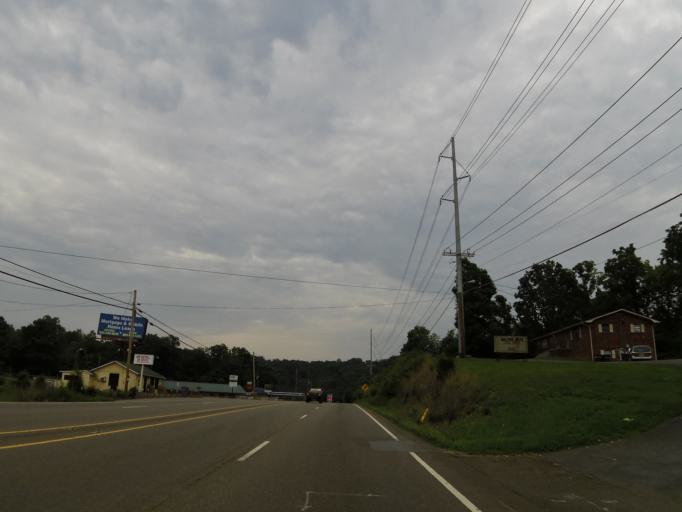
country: US
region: Tennessee
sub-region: Sevier County
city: Seymour
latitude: 35.8997
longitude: -83.8169
